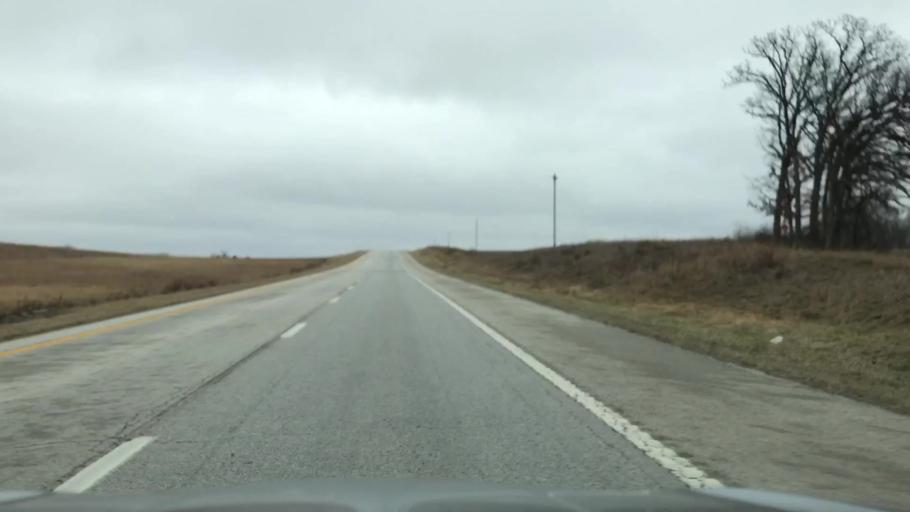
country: US
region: Missouri
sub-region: Linn County
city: Marceline
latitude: 39.7602
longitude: -92.9228
